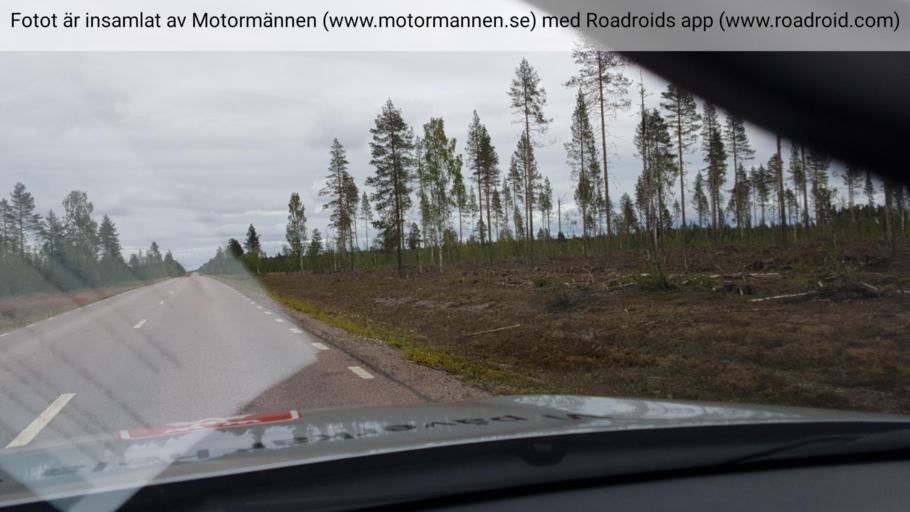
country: SE
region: Norrbotten
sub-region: Overkalix Kommun
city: OEverkalix
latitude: 67.0864
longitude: 22.5539
